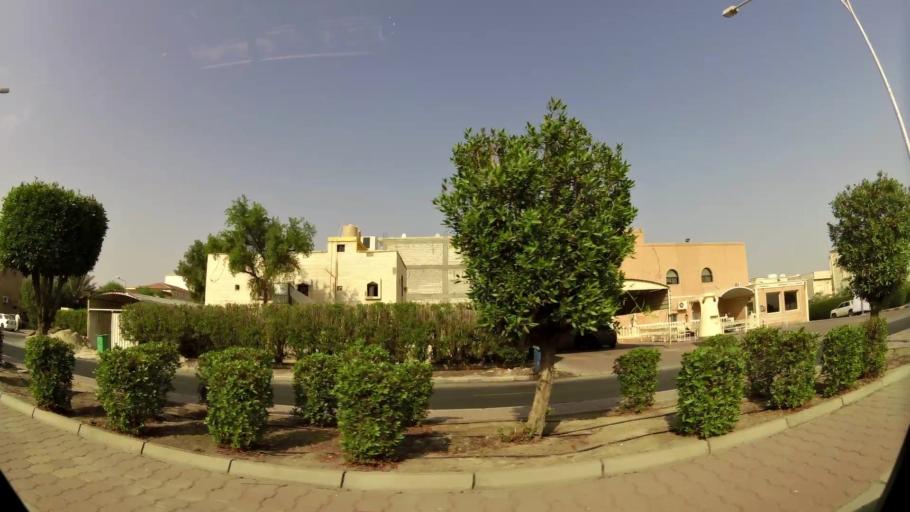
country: KW
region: Muhafazat al Jahra'
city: Al Jahra'
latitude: 29.3328
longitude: 47.7039
